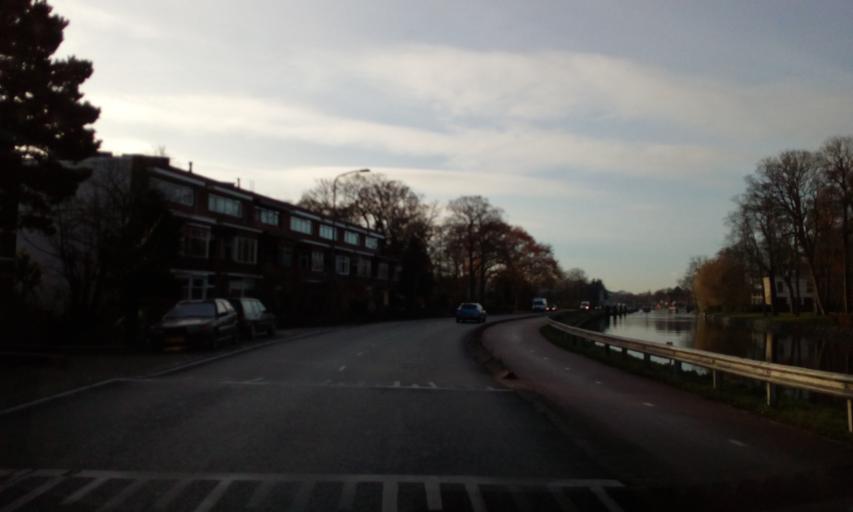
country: NL
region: South Holland
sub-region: Gemeente Leidschendam-Voorburg
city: Voorburg
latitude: 52.0586
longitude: 4.3515
